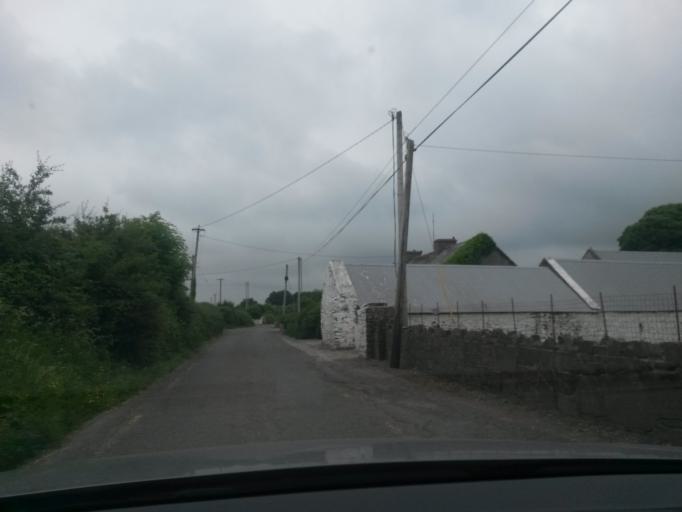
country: IE
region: Munster
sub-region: Ciarrai
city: Tralee
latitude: 52.3796
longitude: -9.7027
